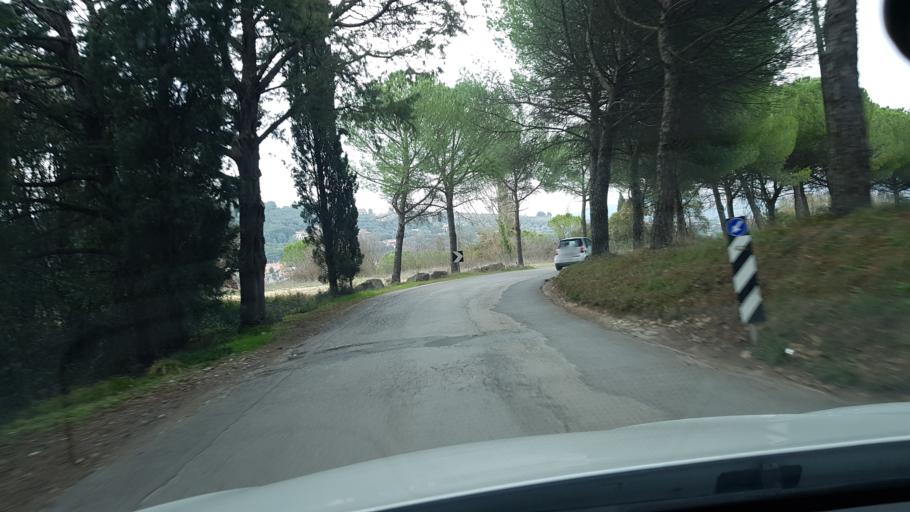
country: IT
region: Umbria
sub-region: Provincia di Perugia
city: Lacugnano
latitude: 43.1032
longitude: 12.3330
